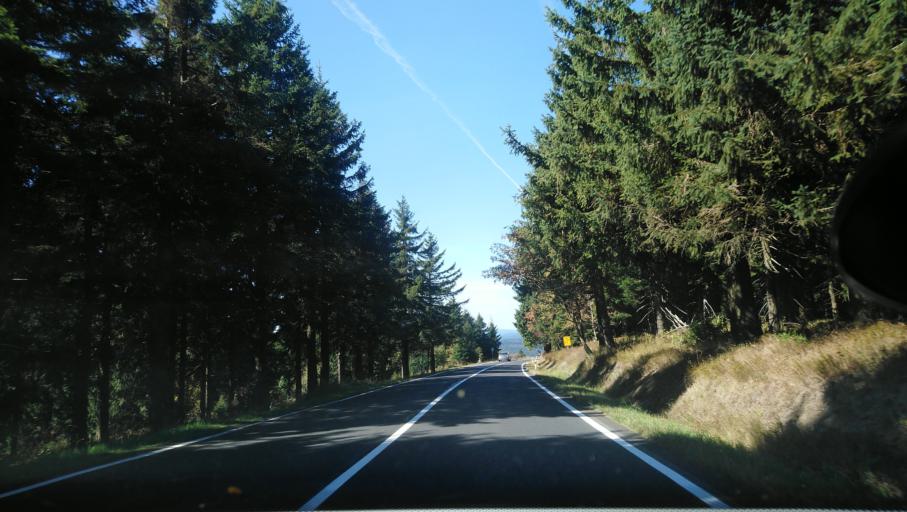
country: DE
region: Saxony
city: Kurort Oberwiesenthal
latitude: 50.4018
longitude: 12.9487
